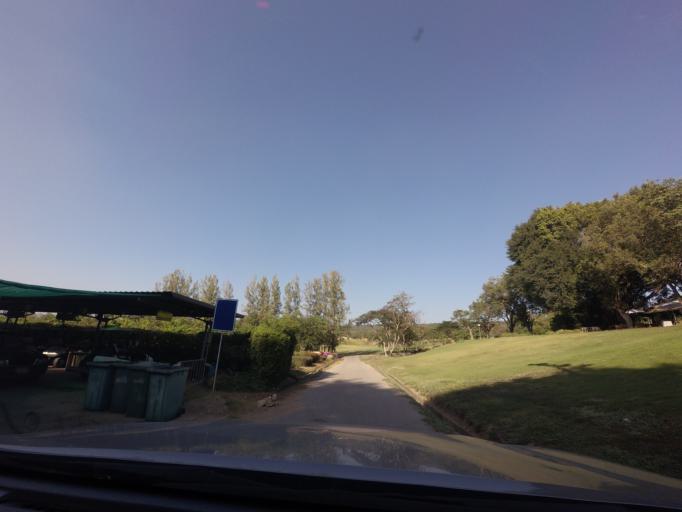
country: TH
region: Lampang
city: Mae Mo
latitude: 18.3225
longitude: 99.7443
